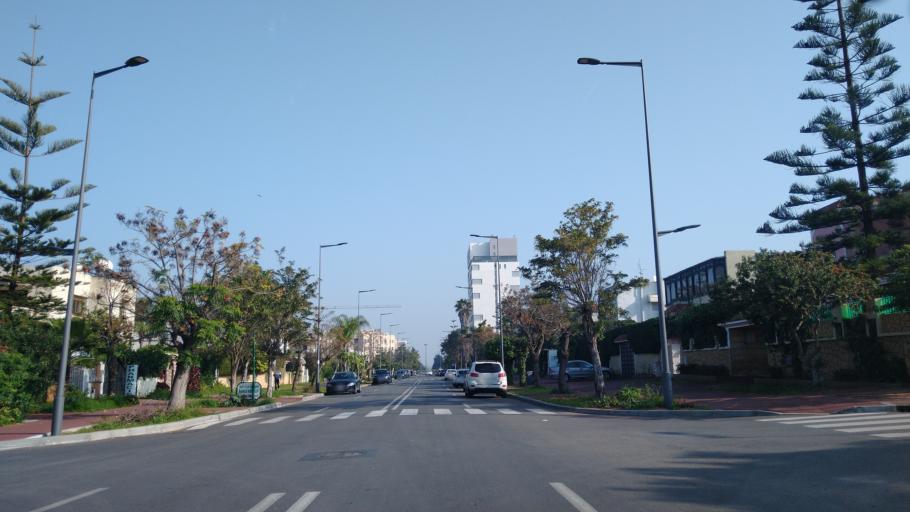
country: MA
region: Rabat-Sale-Zemmour-Zaer
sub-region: Skhirate-Temara
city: Temara
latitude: 33.9530
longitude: -6.8696
